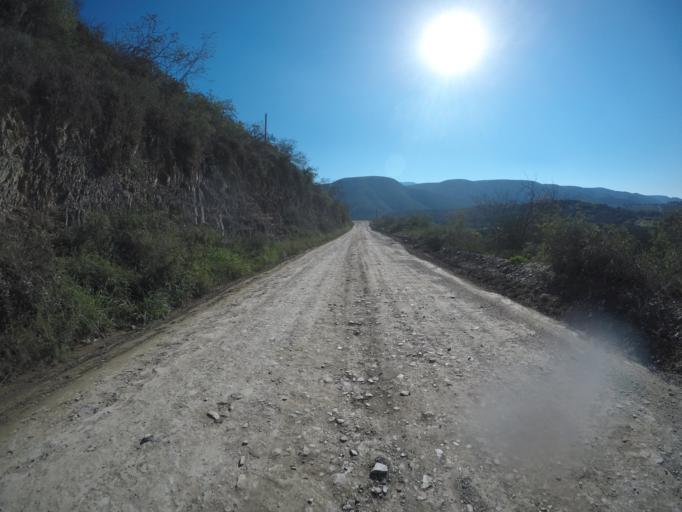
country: ZA
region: Eastern Cape
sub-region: Cacadu District Municipality
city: Kruisfontein
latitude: -33.6657
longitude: 24.5676
